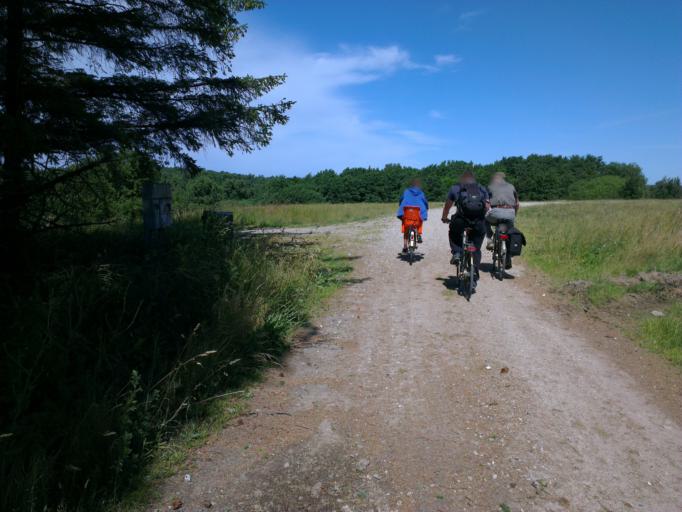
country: DK
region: Capital Region
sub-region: Frederikssund Kommune
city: Jaegerspris
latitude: 55.8823
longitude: 11.9475
